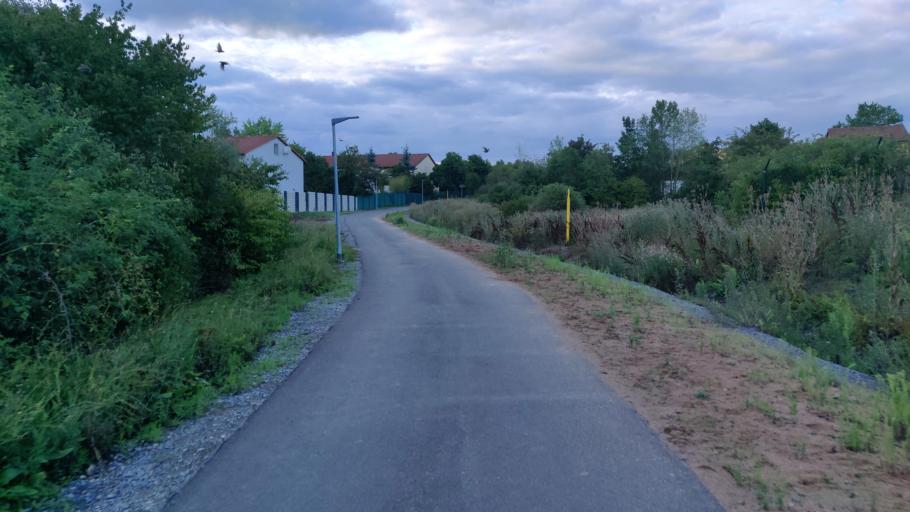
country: DE
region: Bavaria
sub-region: Regierungsbezirk Unterfranken
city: Niederwerrn
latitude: 50.0580
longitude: 10.1988
